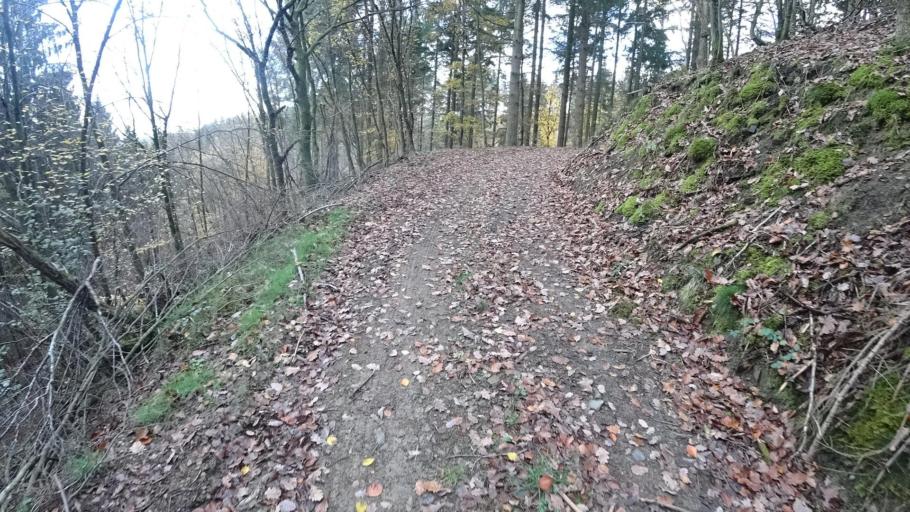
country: DE
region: Rheinland-Pfalz
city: Harscheid
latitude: 50.4669
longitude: 6.8926
